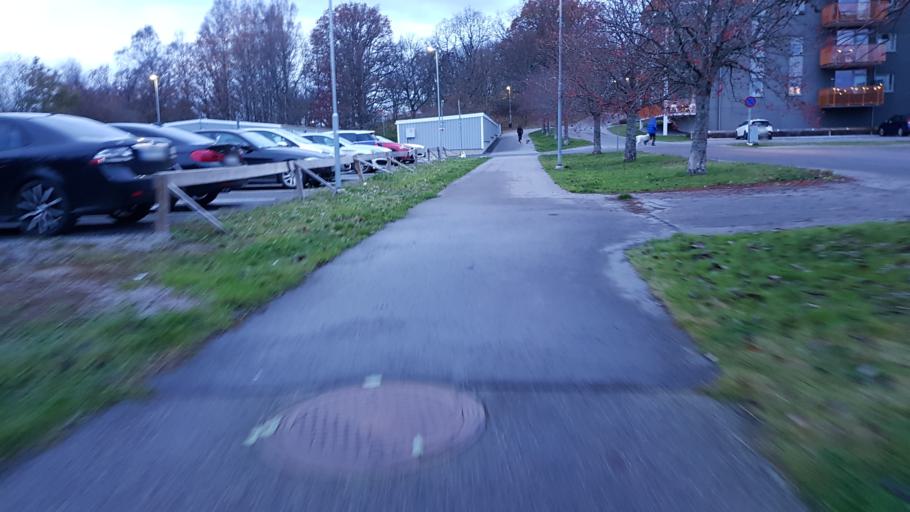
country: SE
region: OEstergoetland
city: Lindo
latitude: 58.6013
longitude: 16.2454
